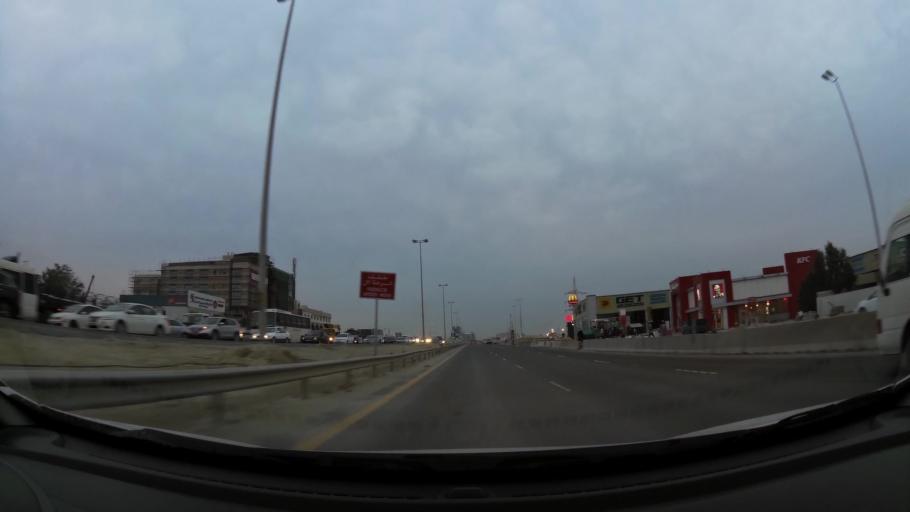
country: BH
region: Northern
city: Ar Rifa'
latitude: 26.1261
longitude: 50.5898
